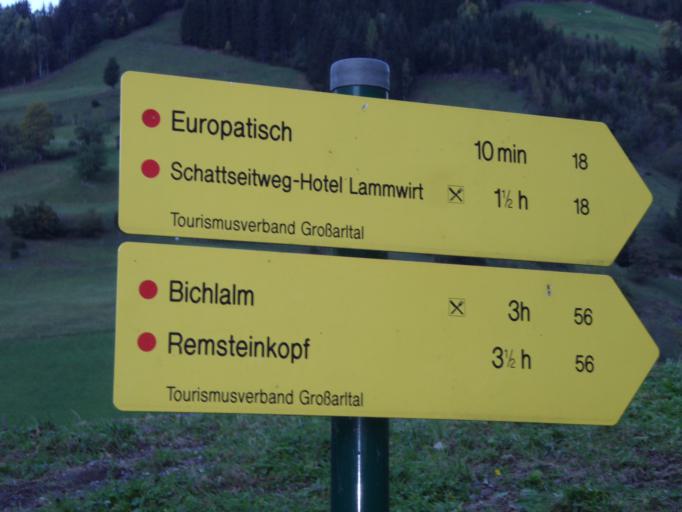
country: AT
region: Salzburg
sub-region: Politischer Bezirk Sankt Johann im Pongau
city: Huttschlag
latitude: 47.2362
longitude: 13.2033
